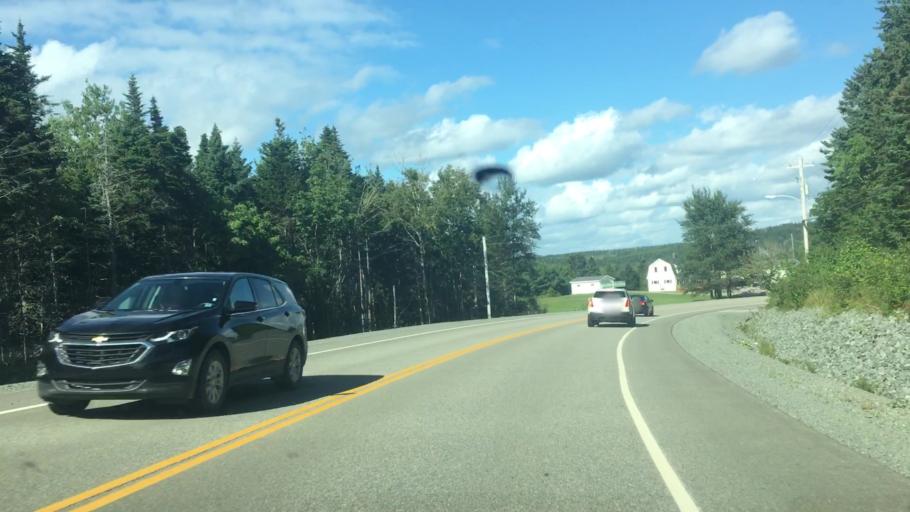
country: CA
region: Nova Scotia
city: Princeville
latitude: 45.6899
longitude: -60.7521
